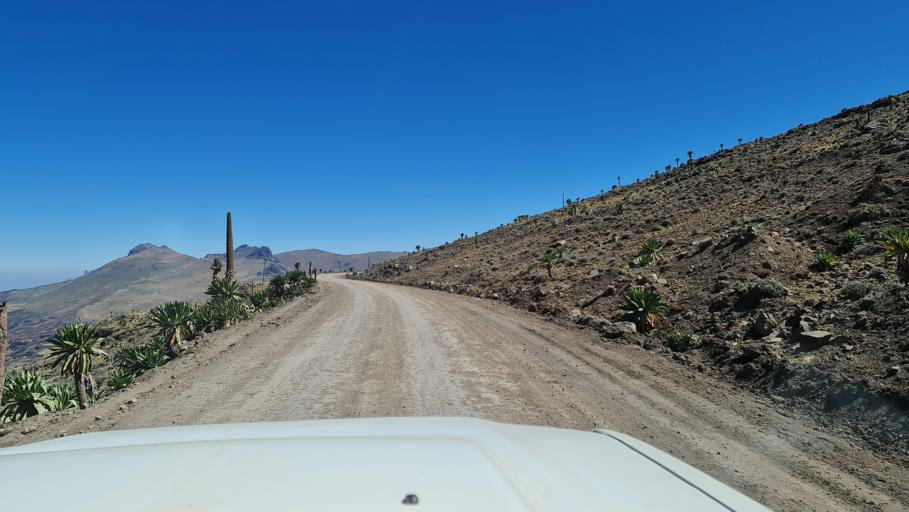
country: ET
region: Amhara
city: Debark'
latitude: 13.2508
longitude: 38.2098
